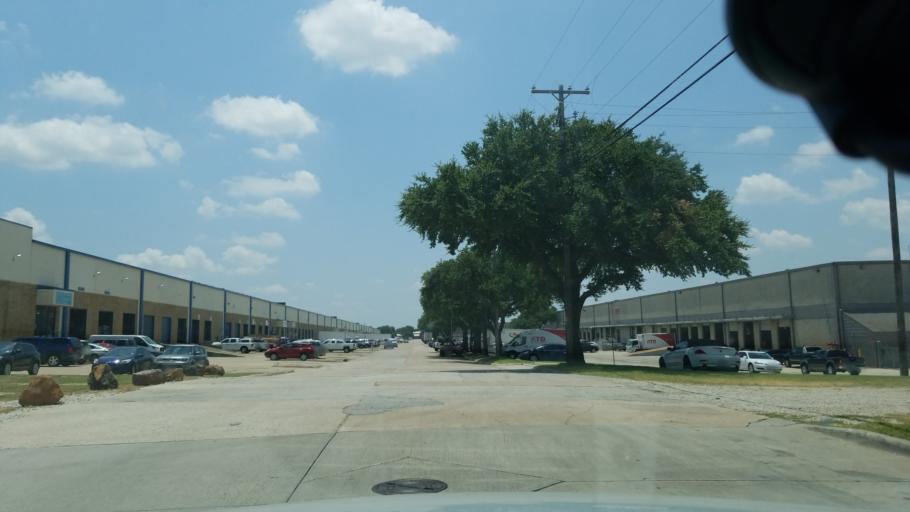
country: US
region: Texas
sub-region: Dallas County
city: Carrollton
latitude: 32.9597
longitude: -96.8795
